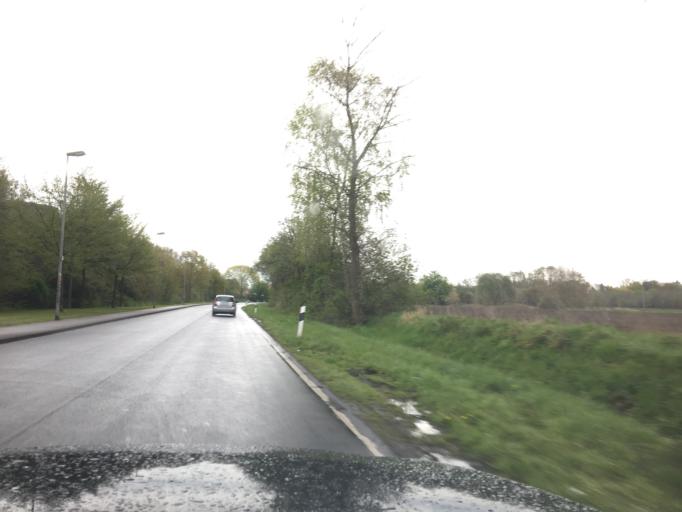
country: DE
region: North Rhine-Westphalia
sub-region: Regierungsbezirk Munster
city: Muenster
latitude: 51.9894
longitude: 7.6185
